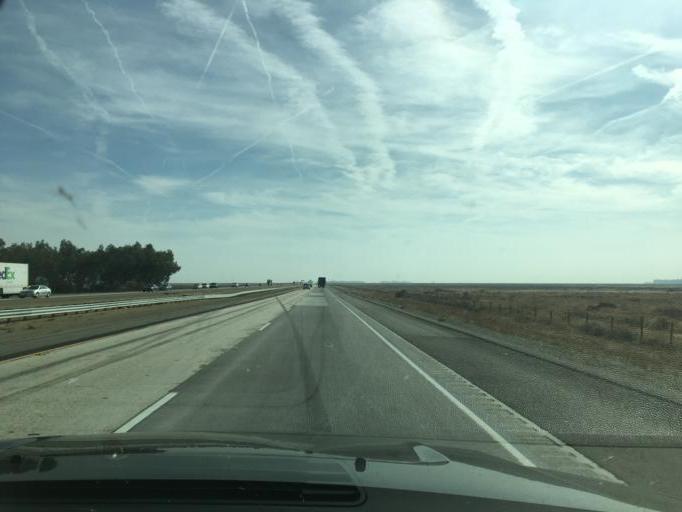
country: US
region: California
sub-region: Kern County
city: Lost Hills
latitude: 35.5969
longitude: -119.6371
